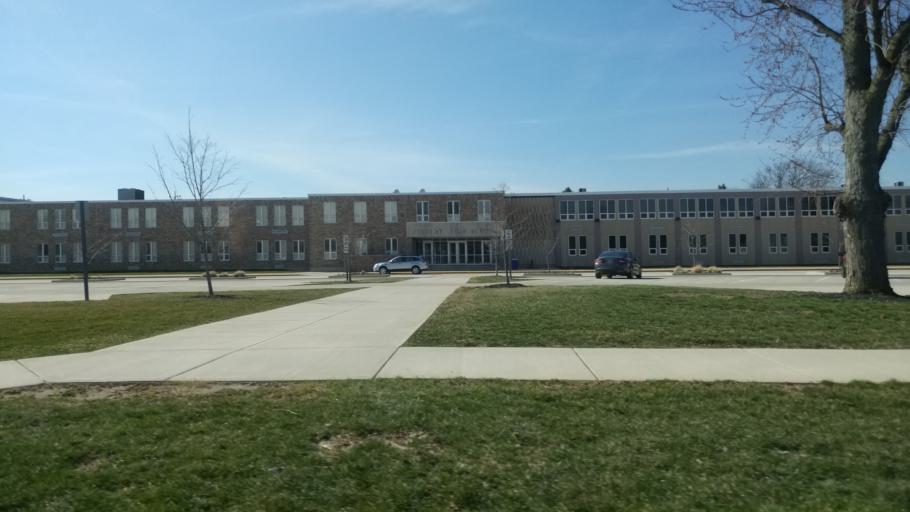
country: US
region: Ohio
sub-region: Hancock County
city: Findlay
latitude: 41.0554
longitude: -83.6646
